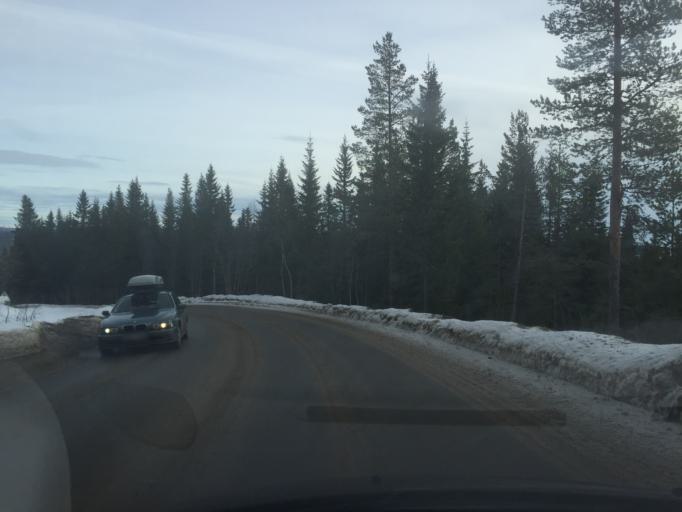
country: NO
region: Hedmark
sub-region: Trysil
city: Innbygda
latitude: 61.3371
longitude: 12.1851
